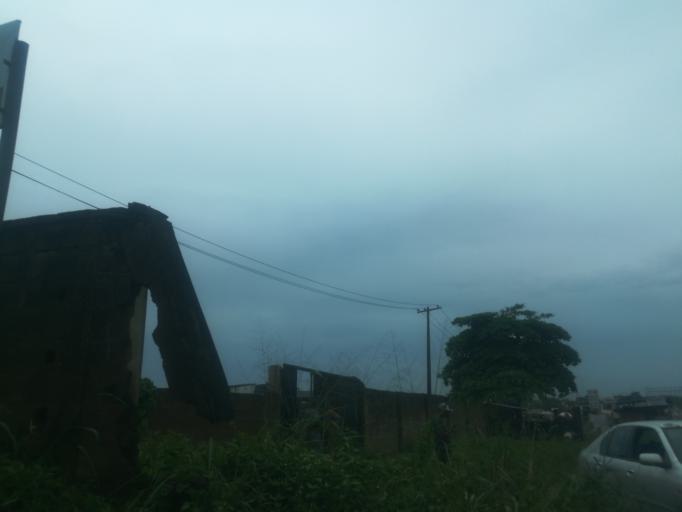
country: NG
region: Oyo
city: Ibadan
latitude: 7.3366
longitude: 3.8930
